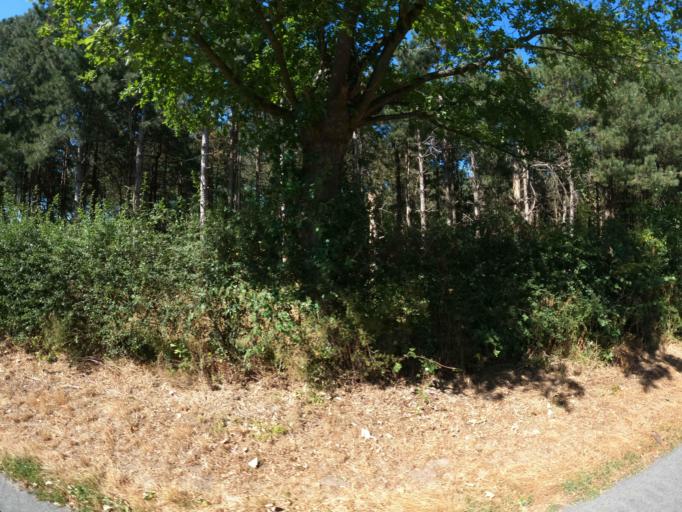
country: FR
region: Pays de la Loire
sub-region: Departement de la Vendee
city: Les Landes-Genusson
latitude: 46.9640
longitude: -1.1090
